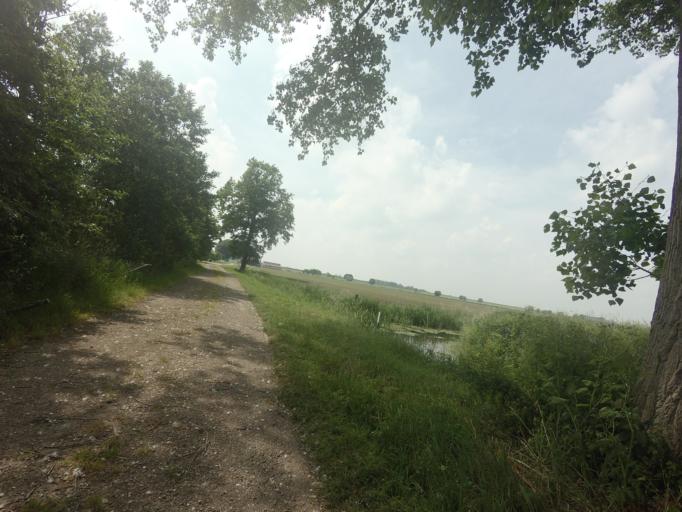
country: NL
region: Gelderland
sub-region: Gemeente Culemborg
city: Culemborg
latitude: 51.9797
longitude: 5.2698
